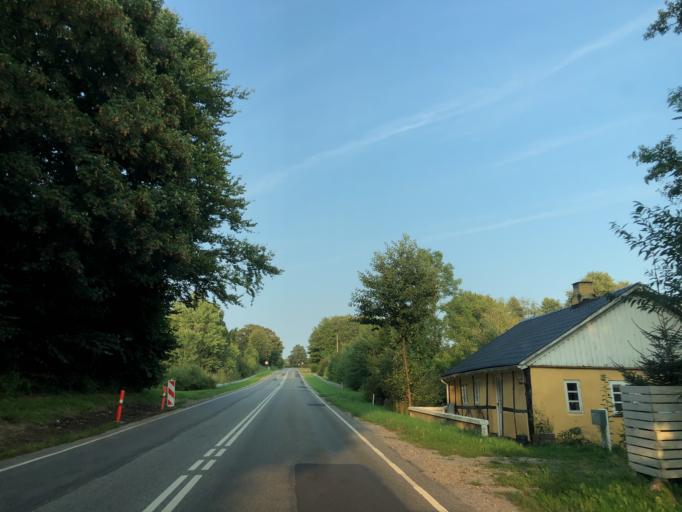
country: DK
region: South Denmark
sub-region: Vejle Kommune
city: Jelling
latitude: 55.7099
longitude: 9.4669
